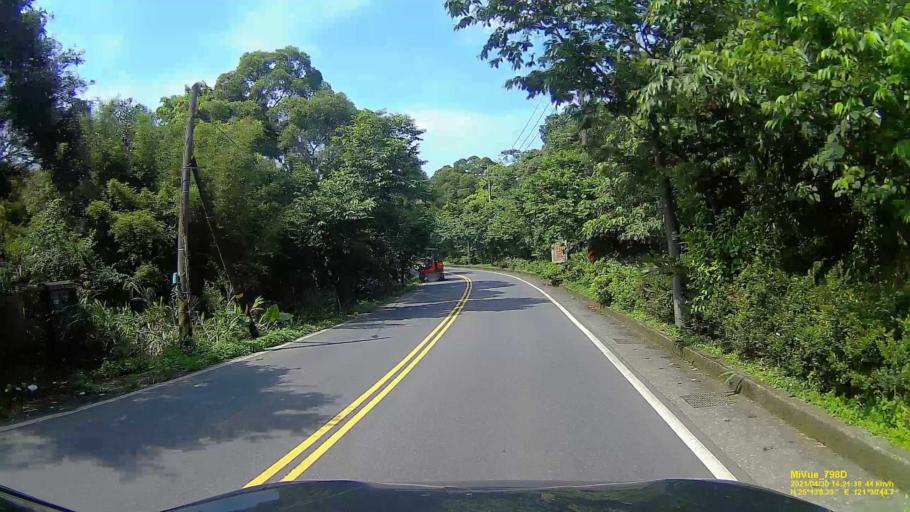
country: TW
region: Taipei
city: Taipei
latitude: 25.2191
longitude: 121.5124
